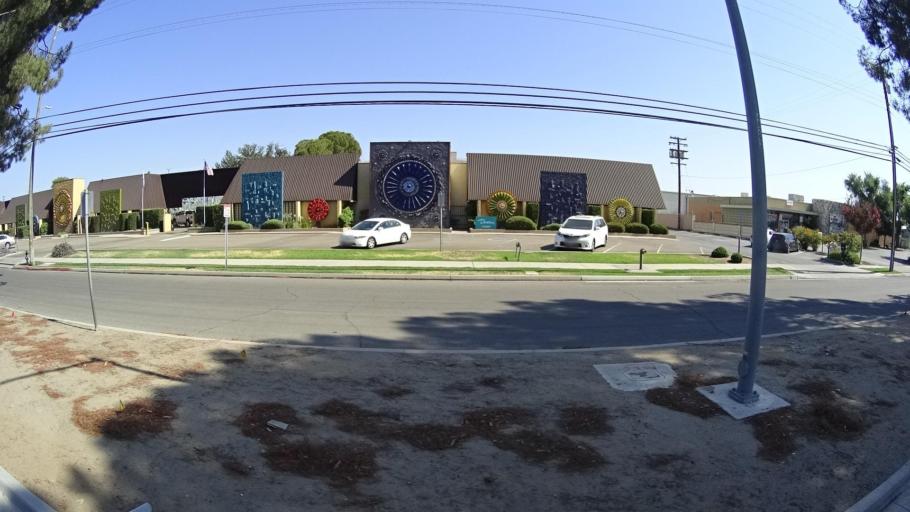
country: US
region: California
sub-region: Fresno County
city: Tarpey Village
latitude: 36.7795
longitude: -119.6969
